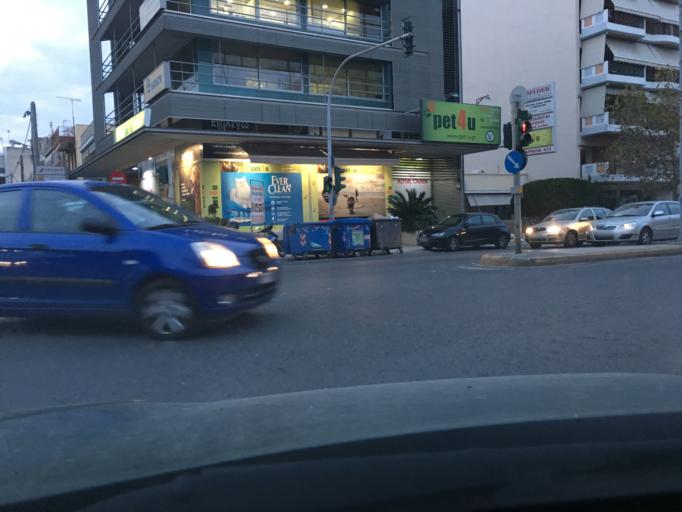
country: GR
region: Attica
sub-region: Nomarchia Athinas
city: Nea Chalkidona
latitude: 38.0286
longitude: 23.7306
